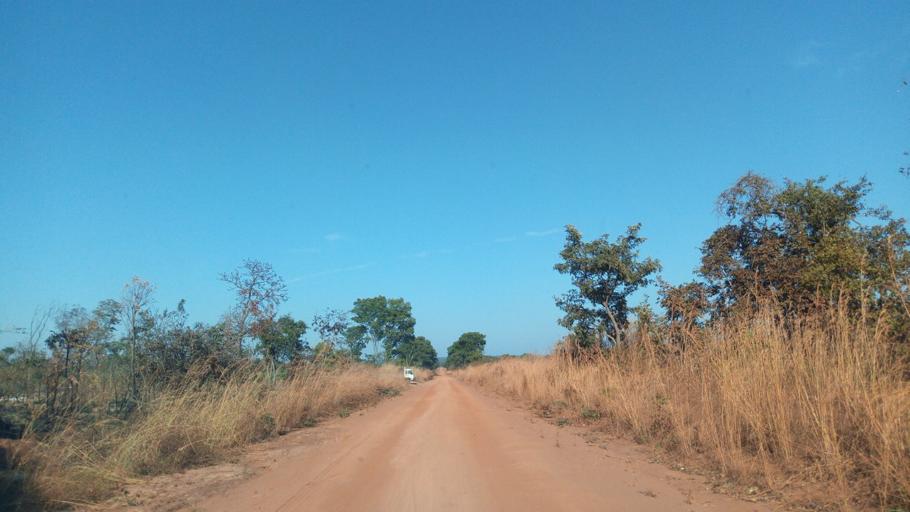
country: ZM
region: Luapula
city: Mwense
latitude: -10.5915
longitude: 28.4362
